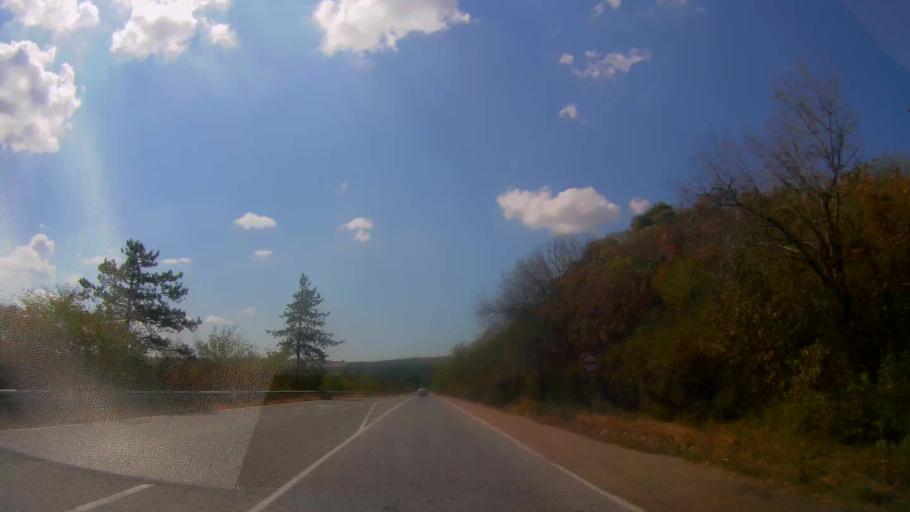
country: BG
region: Veliko Turnovo
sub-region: Obshtina Polski Trumbesh
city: Polski Trumbesh
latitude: 43.4468
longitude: 25.6575
